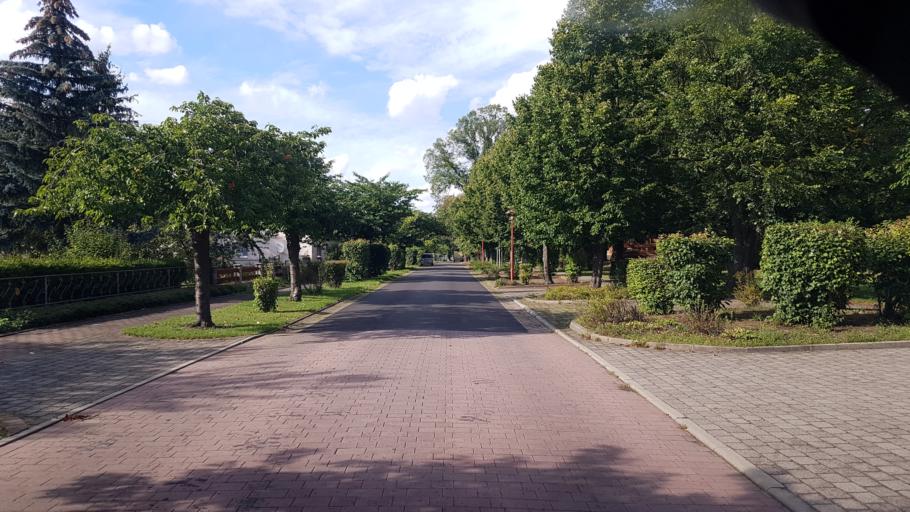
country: DE
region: Saxony
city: Schleife
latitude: 51.5731
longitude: 14.4739
